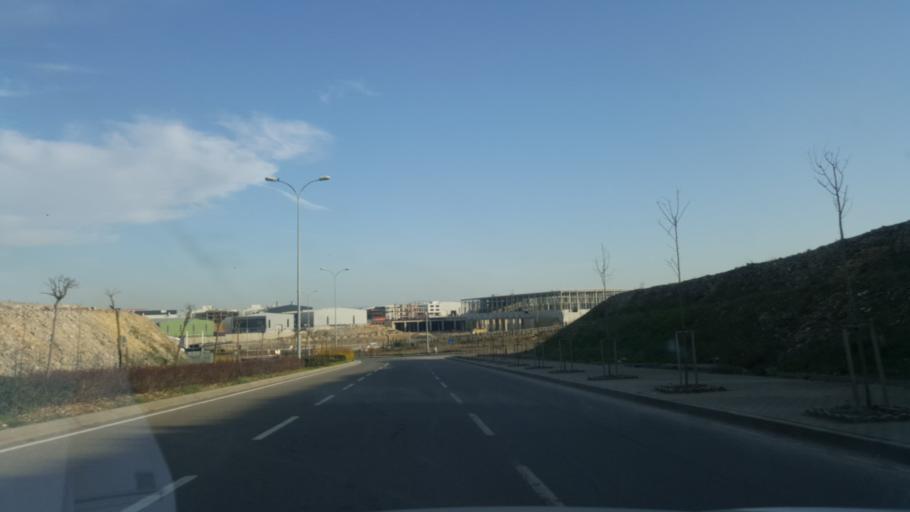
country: TR
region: Kocaeli
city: Tavsanli
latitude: 40.8297
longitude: 29.5587
